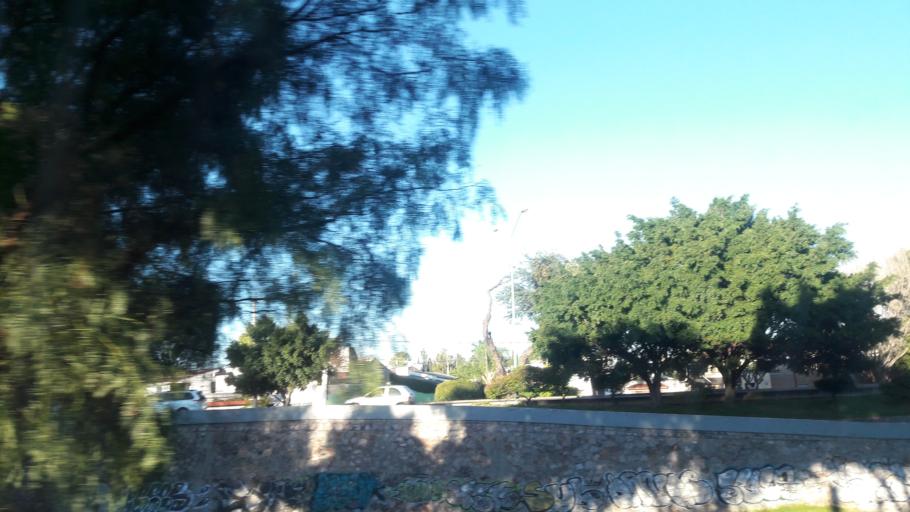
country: MX
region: Guanajuato
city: Leon
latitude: 21.1075
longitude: -101.6622
